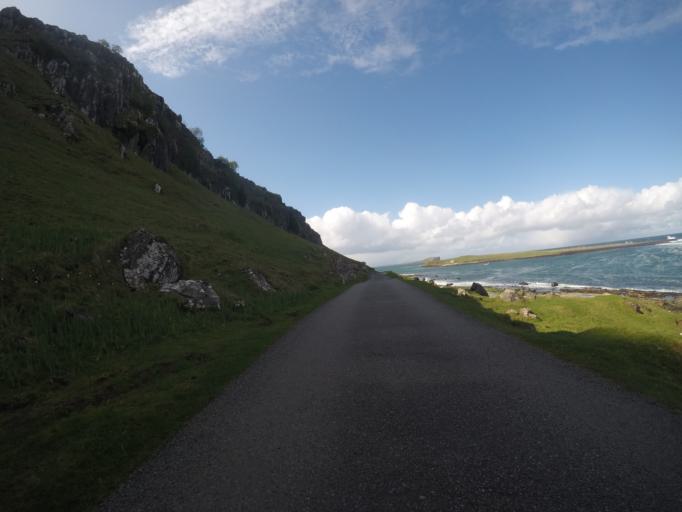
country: GB
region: Scotland
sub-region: Highland
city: Portree
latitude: 57.6346
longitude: -6.2026
